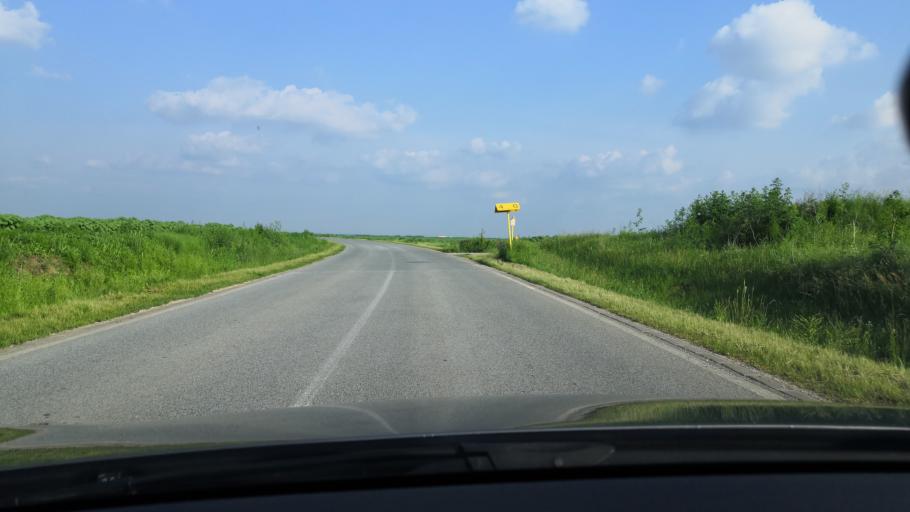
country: RS
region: Autonomna Pokrajina Vojvodina
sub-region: Sremski Okrug
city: Ingija
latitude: 45.0904
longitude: 20.0981
